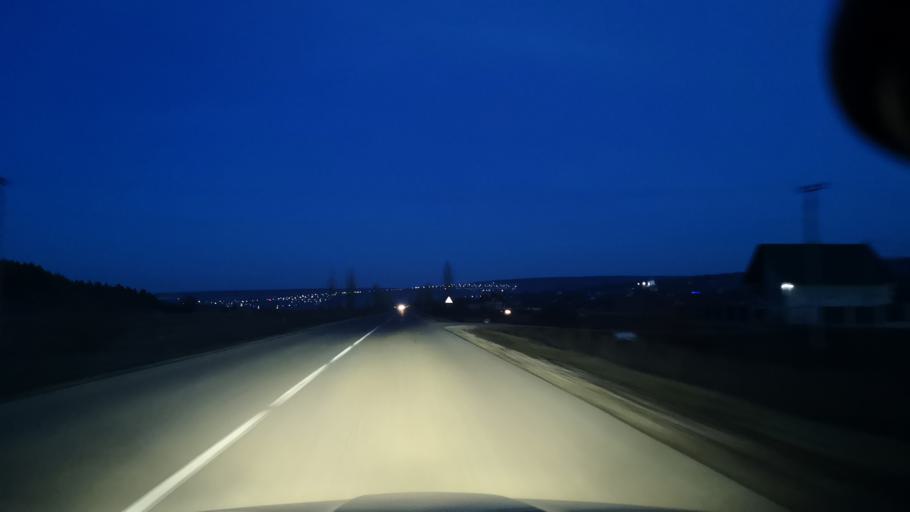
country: MD
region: Orhei
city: Orhei
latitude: 47.3437
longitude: 28.7517
